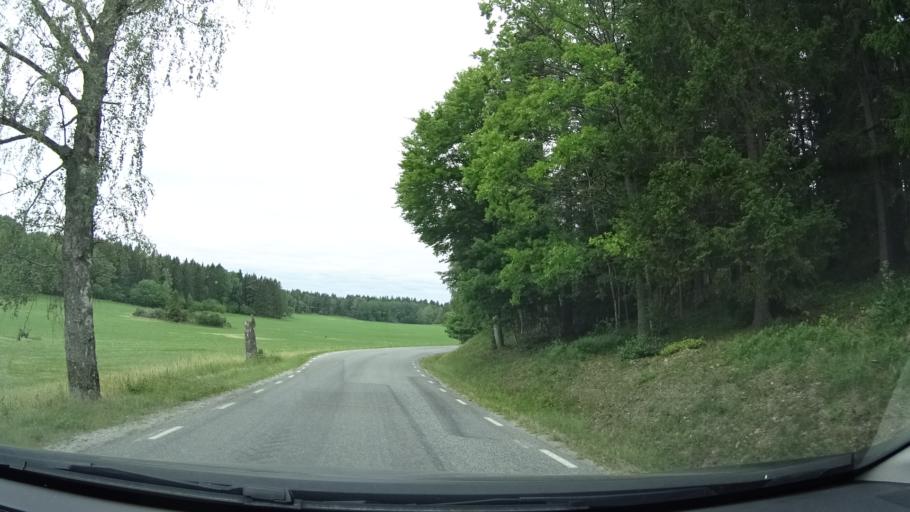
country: SE
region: Stockholm
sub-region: Varmdo Kommun
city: Mortnas
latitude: 59.3651
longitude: 18.4717
